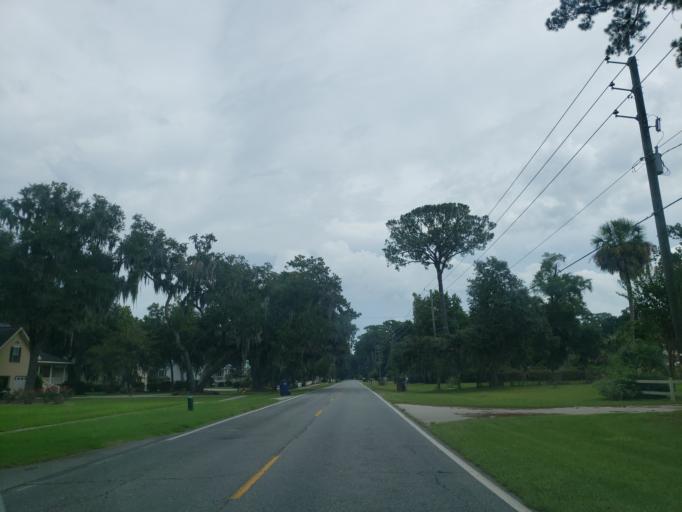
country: US
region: Georgia
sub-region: Chatham County
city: Wilmington Island
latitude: 31.9977
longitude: -80.9730
